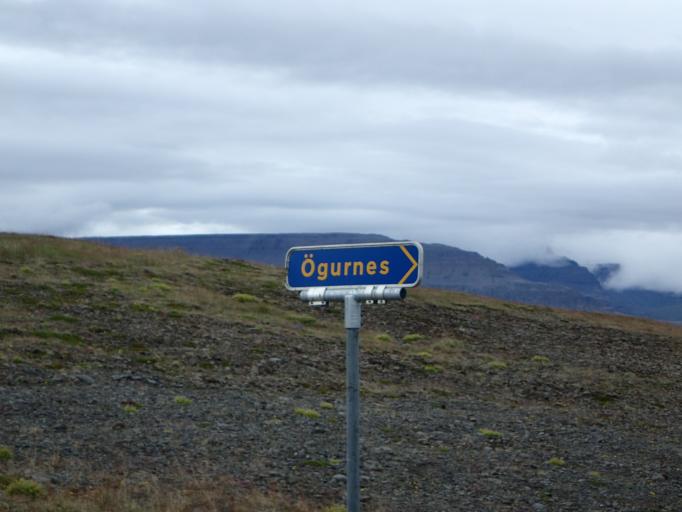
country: IS
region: Westfjords
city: Isafjoerdur
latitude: 66.0544
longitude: -22.7598
